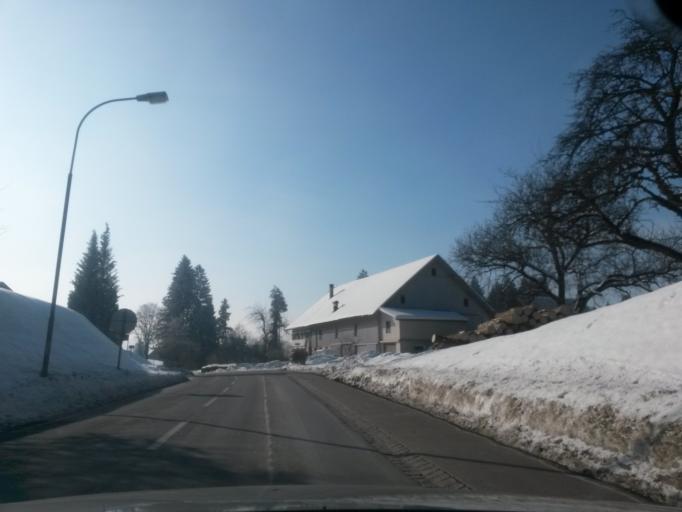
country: DE
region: Bavaria
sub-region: Swabia
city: Sigmarszell
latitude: 47.5771
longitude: 9.7747
